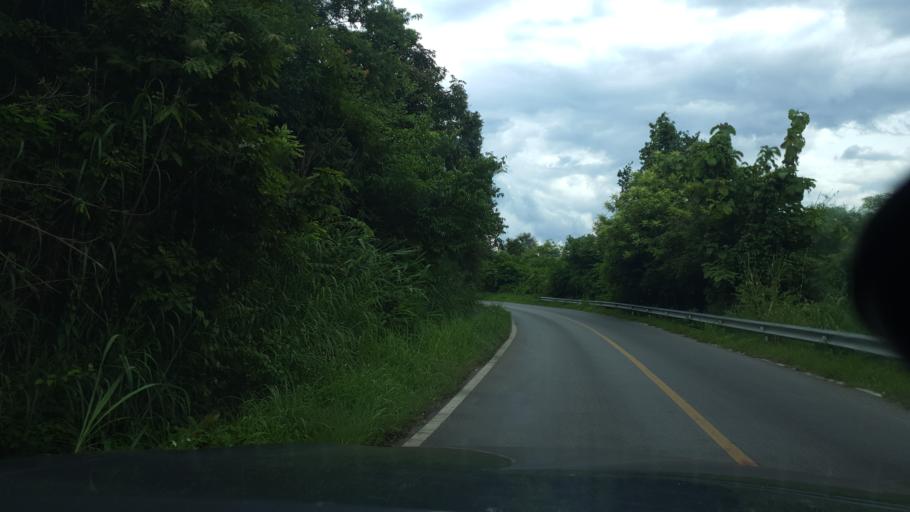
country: TH
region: Lamphun
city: Mae Tha
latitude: 18.5263
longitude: 99.2267
